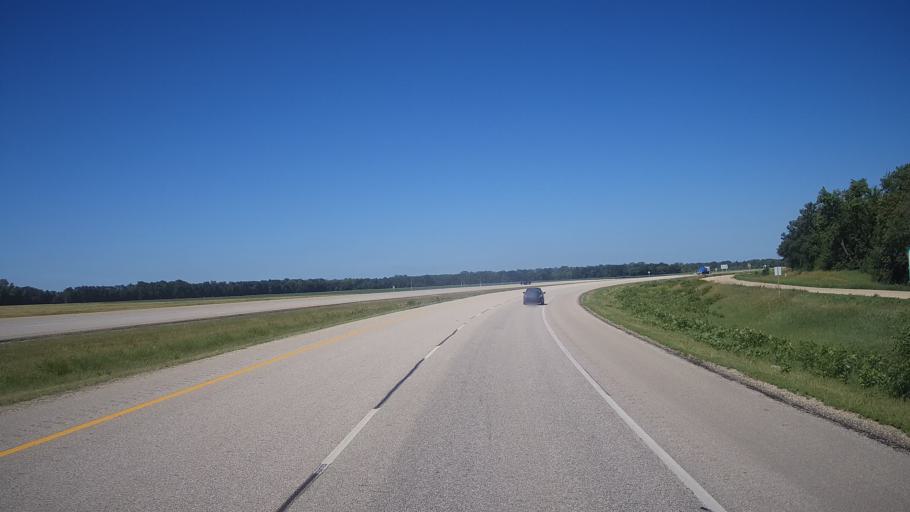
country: CA
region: Manitoba
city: Portage la Prairie
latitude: 49.9464
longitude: -98.2972
